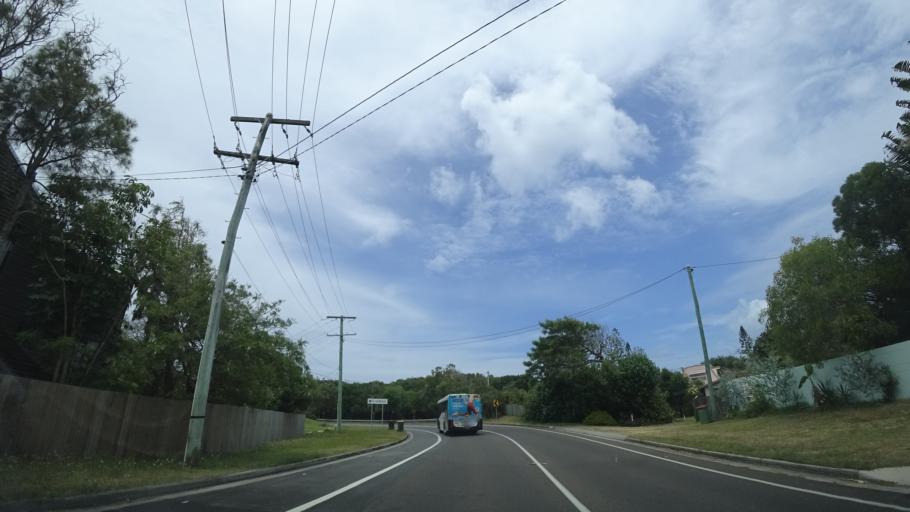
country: AU
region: Queensland
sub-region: Sunshine Coast
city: Coolum Beach
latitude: -26.5496
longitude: 153.0996
